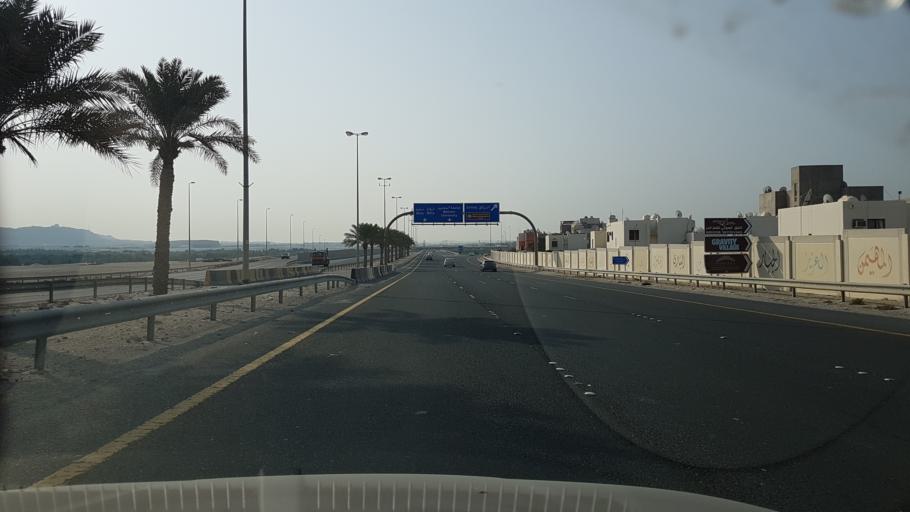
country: BH
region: Central Governorate
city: Dar Kulayb
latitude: 26.0651
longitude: 50.5165
